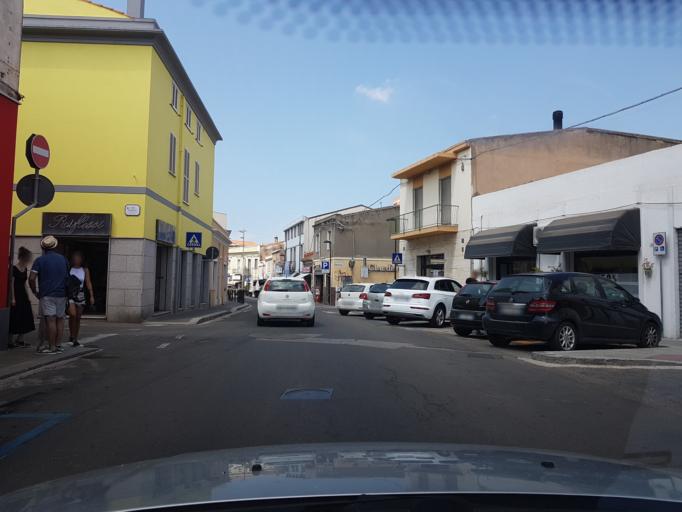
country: IT
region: Sardinia
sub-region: Provincia di Oristano
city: Oristano
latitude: 39.9068
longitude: 8.5933
